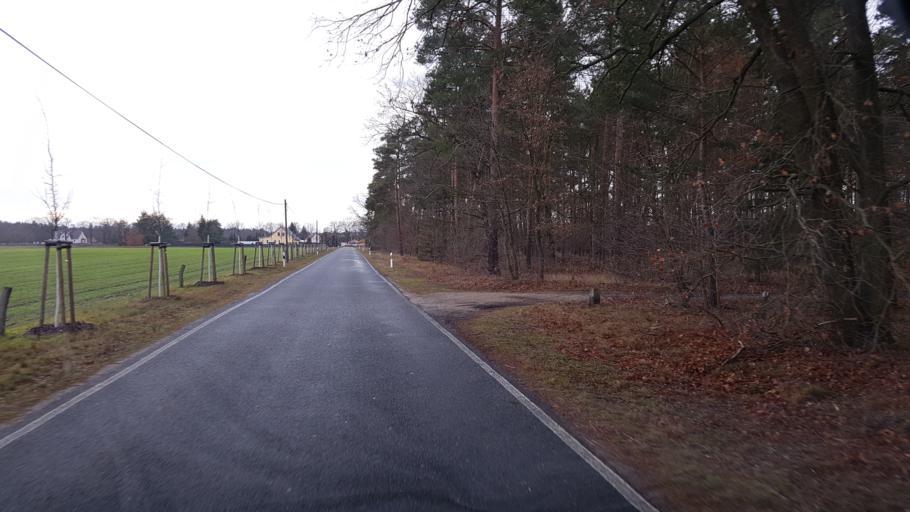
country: DE
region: Brandenburg
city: Altdobern
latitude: 51.6872
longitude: 14.0306
